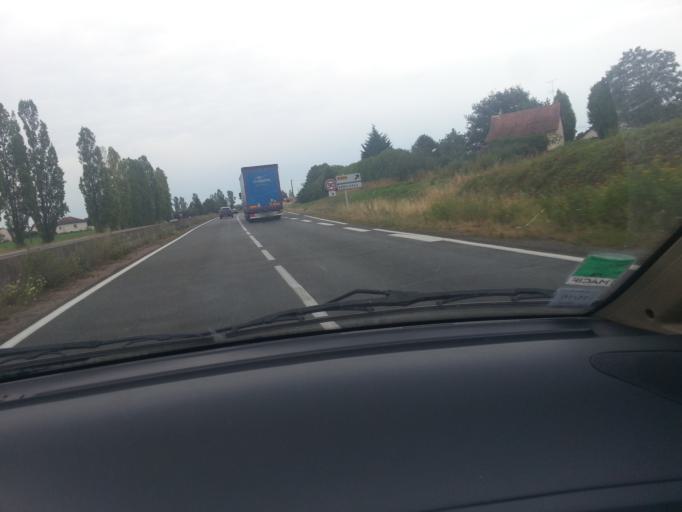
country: FR
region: Bourgogne
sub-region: Departement de Saone-et-Loire
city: Ciry-le-Noble
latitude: 46.6228
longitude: 4.2936
